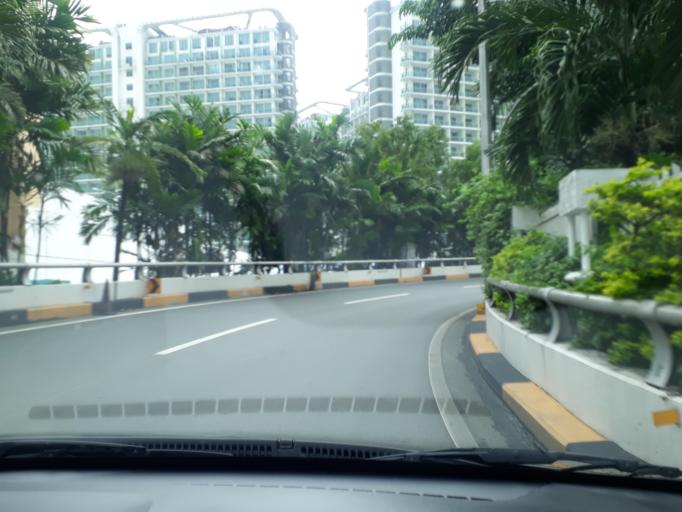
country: PH
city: Sambayanihan People's Village
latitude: 14.4857
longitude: 121.0422
